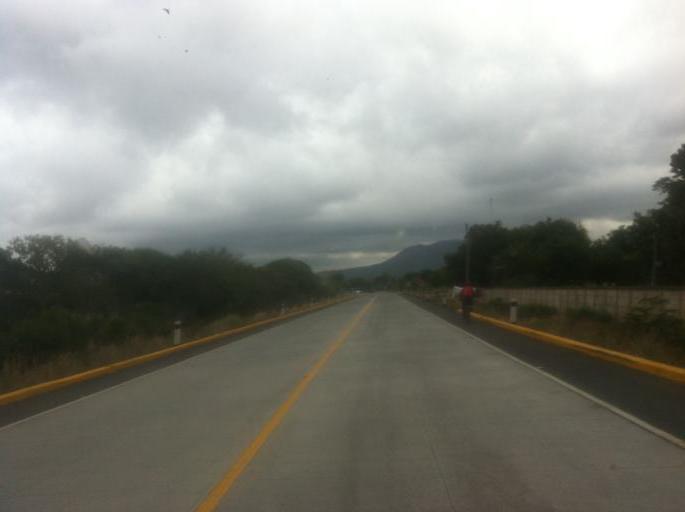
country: NI
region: Masaya
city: Nindiri
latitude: 11.9988
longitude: -86.1052
